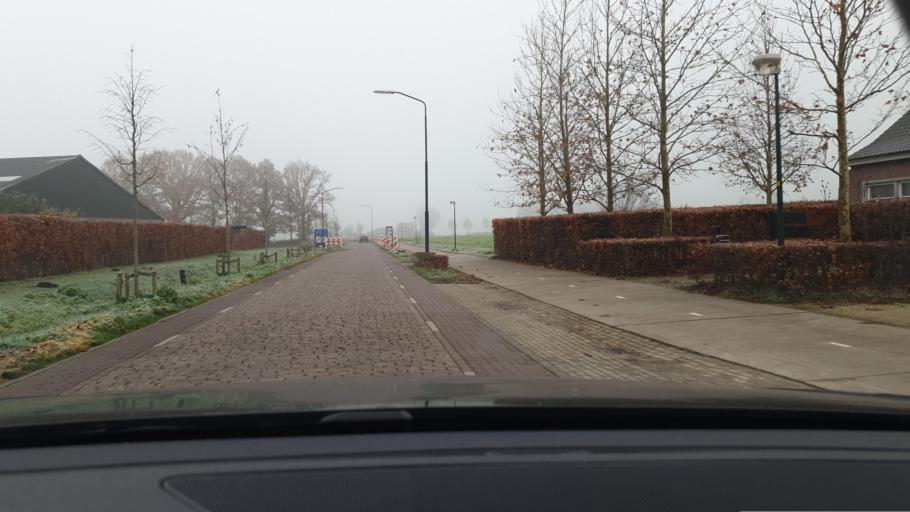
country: NL
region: North Brabant
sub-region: Gemeente Bladel en Netersel
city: Bladel
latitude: 51.4038
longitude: 5.2181
